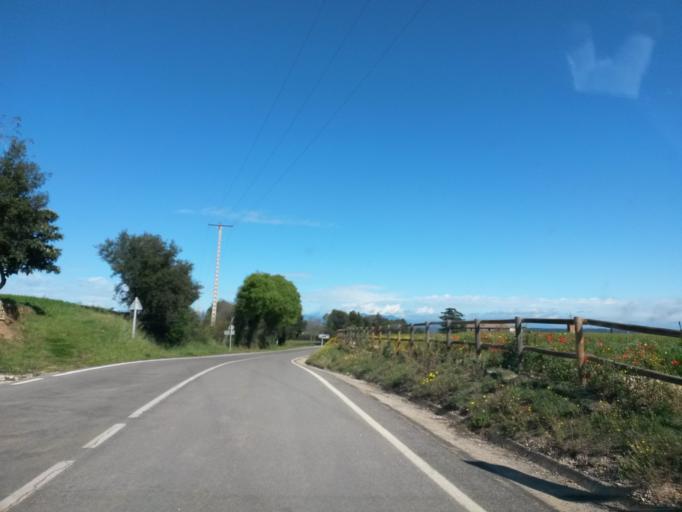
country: ES
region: Catalonia
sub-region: Provincia de Girona
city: Juia
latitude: 42.0190
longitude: 2.9064
